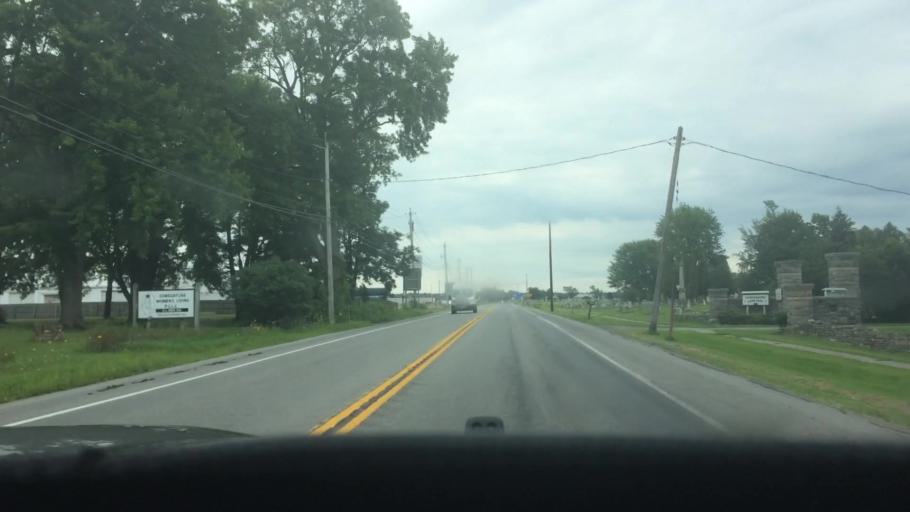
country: US
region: New York
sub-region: St. Lawrence County
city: Ogdensburg
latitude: 44.6831
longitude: -75.4811
